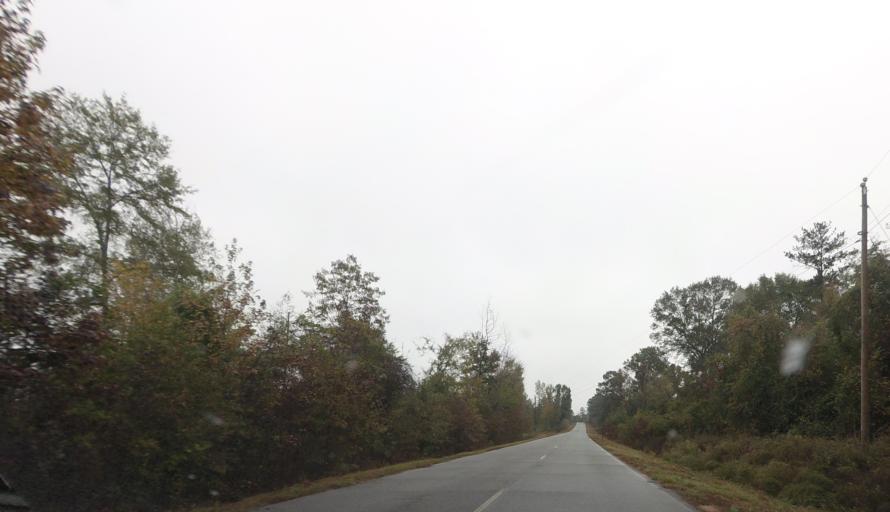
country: US
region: Georgia
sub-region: Macon County
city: Marshallville
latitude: 32.5348
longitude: -83.9919
